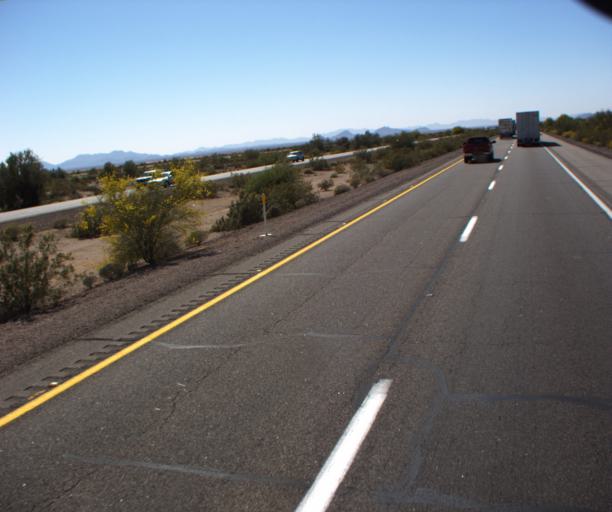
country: US
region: Arizona
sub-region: Yuma County
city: Wellton
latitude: 32.7203
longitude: -113.7780
